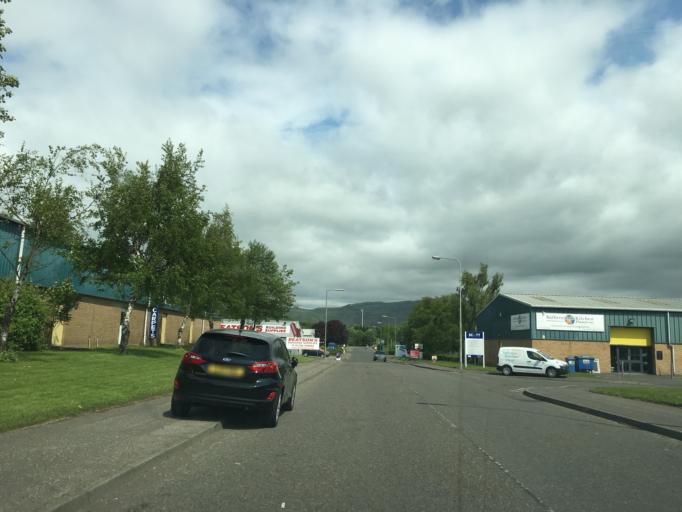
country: GB
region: Scotland
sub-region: Stirling
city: Stirling
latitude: 56.1137
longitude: -3.9142
